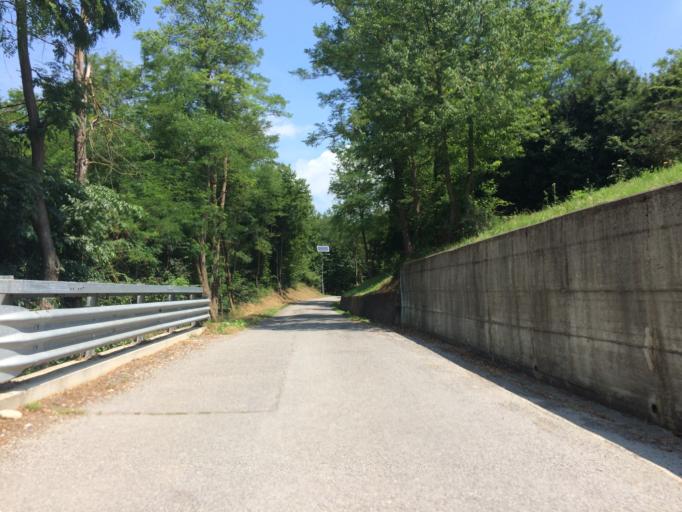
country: IT
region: Piedmont
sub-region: Provincia di Cuneo
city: Bagnasco
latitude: 44.3113
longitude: 8.0572
